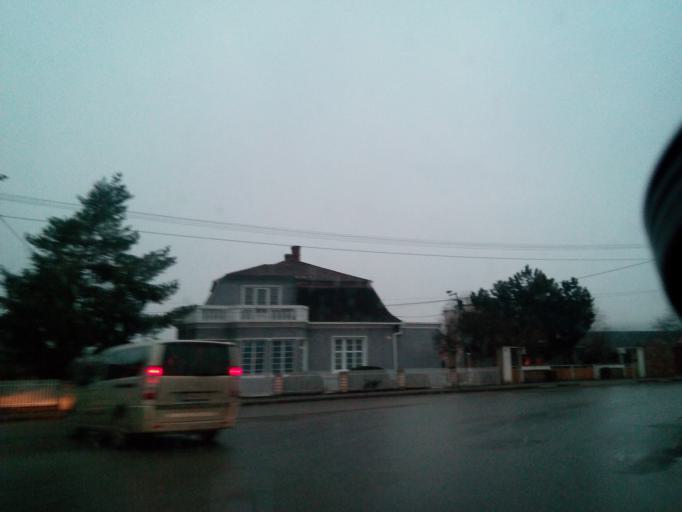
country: SK
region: Presovsky
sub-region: Okres Presov
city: Presov
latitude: 49.0392
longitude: 21.1997
